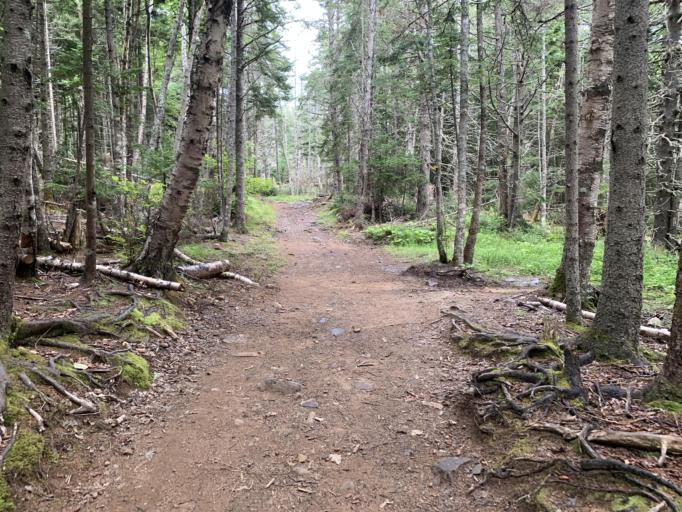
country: CA
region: Nova Scotia
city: Parrsboro
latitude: 45.3166
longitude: -64.4333
